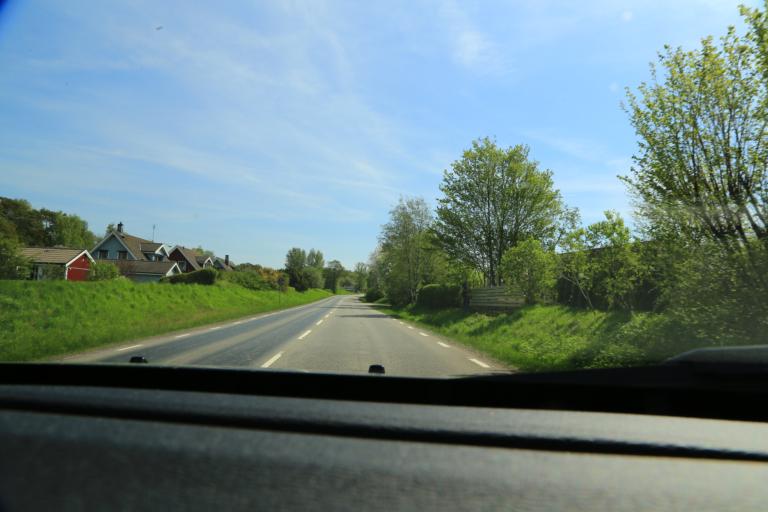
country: SE
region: Halland
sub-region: Varbergs Kommun
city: Varberg
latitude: 57.1417
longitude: 12.2834
